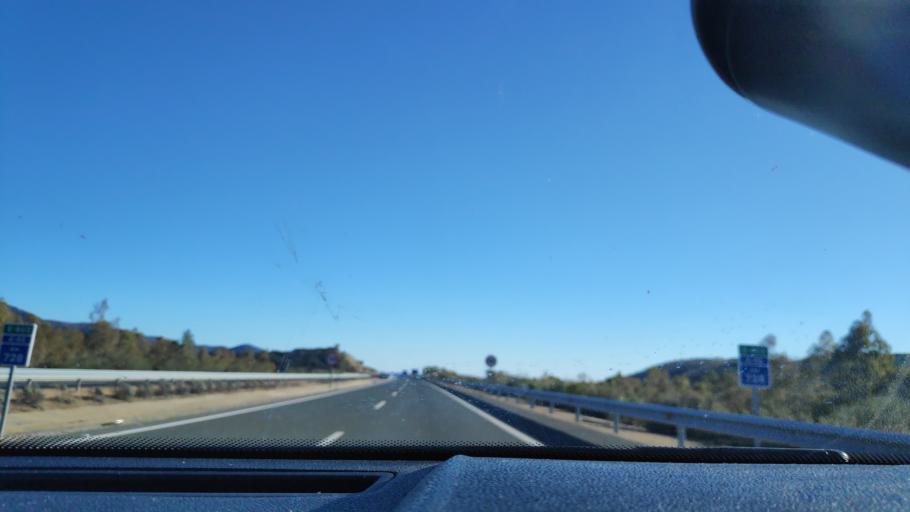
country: ES
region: Extremadura
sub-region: Provincia de Badajoz
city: Monesterio
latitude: 38.0464
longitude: -6.2334
